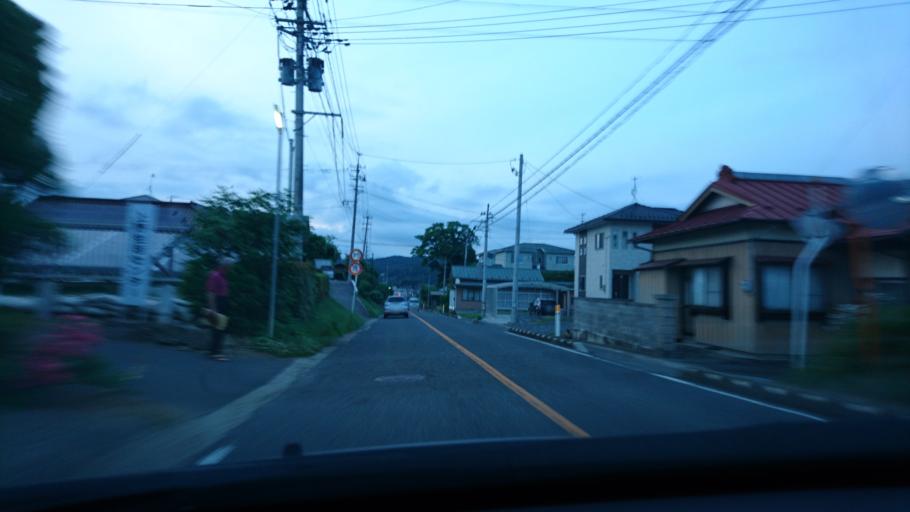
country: JP
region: Iwate
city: Ichinoseki
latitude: 38.8200
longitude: 140.9857
